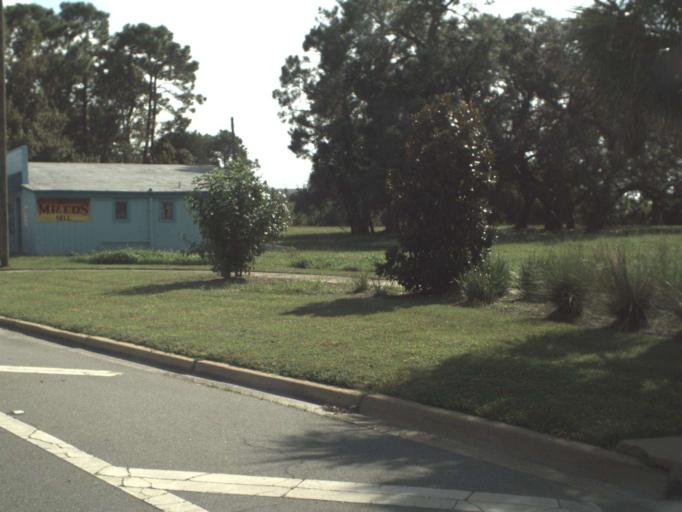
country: US
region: Florida
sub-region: Gulf County
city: Port Saint Joe
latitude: 29.8188
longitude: -85.3062
